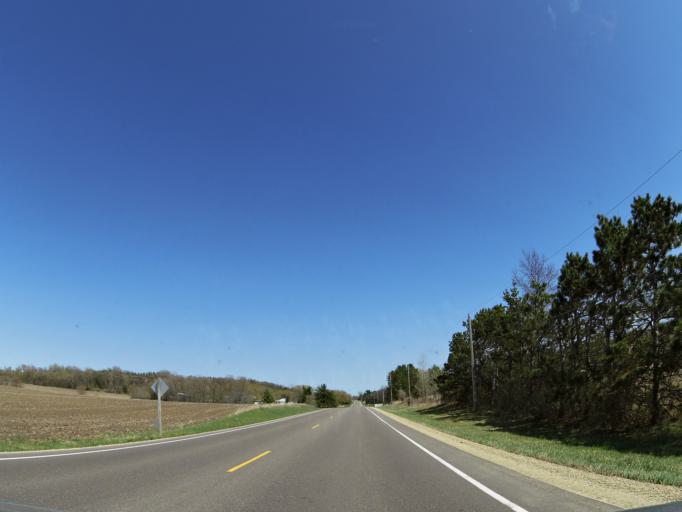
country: US
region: Wisconsin
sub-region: Saint Croix County
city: Hudson
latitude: 44.9599
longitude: -92.6782
